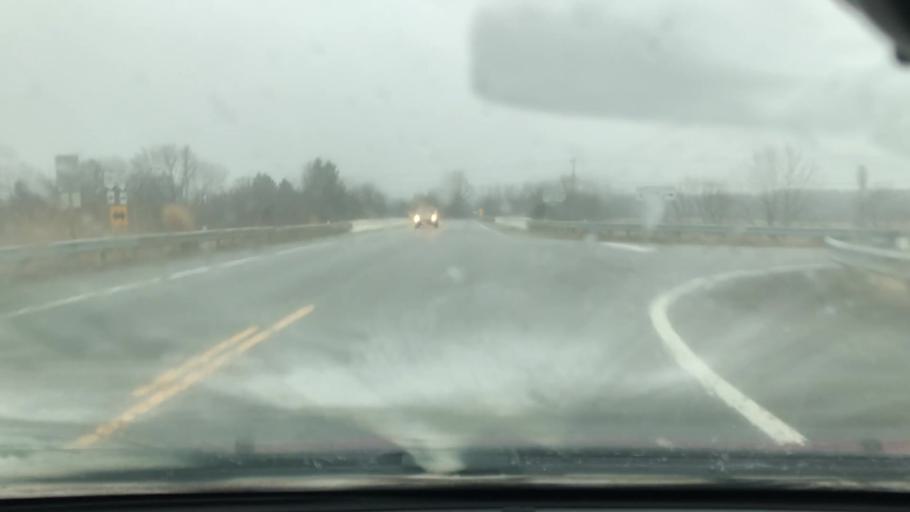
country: US
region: Ohio
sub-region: Wayne County
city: Doylestown
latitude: 40.9559
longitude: -81.7360
